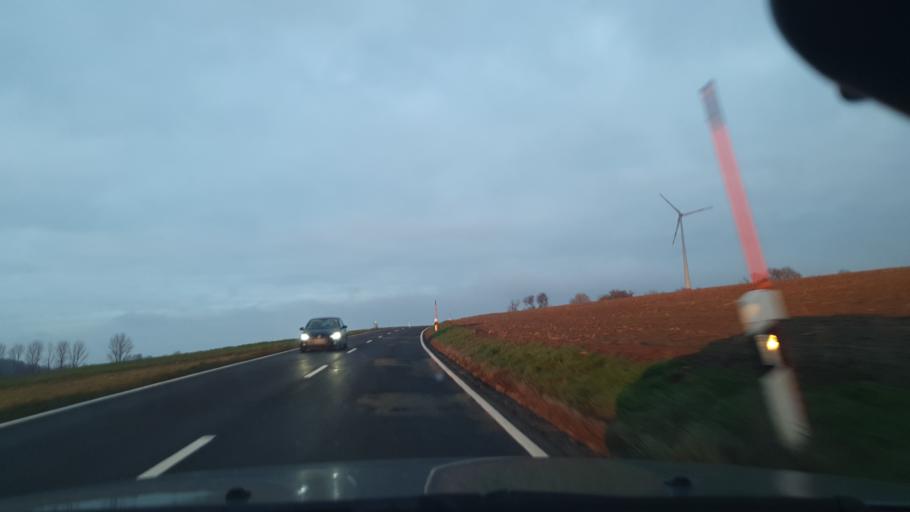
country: DE
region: Rheinland-Pfalz
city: Langwieden
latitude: 49.3734
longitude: 7.5088
